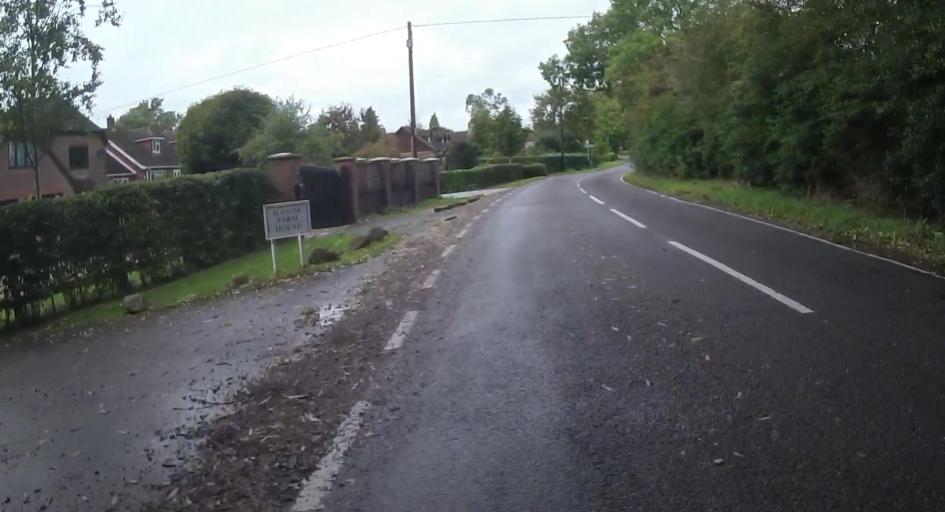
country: GB
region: England
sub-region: Hampshire
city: Tadley
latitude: 51.3436
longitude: -1.1630
